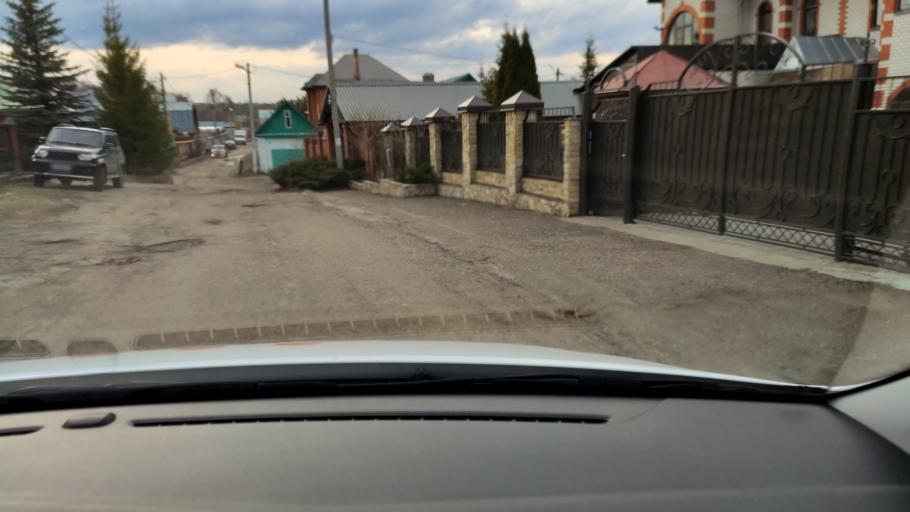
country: RU
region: Tatarstan
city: Stolbishchi
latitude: 55.7417
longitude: 49.2648
